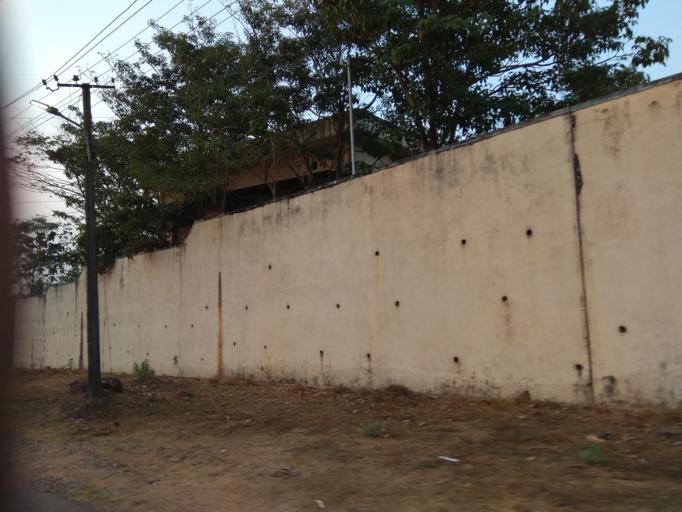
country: IN
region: Karnataka
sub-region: Dakshina Kannada
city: Mangalore
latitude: 12.9283
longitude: 74.8671
